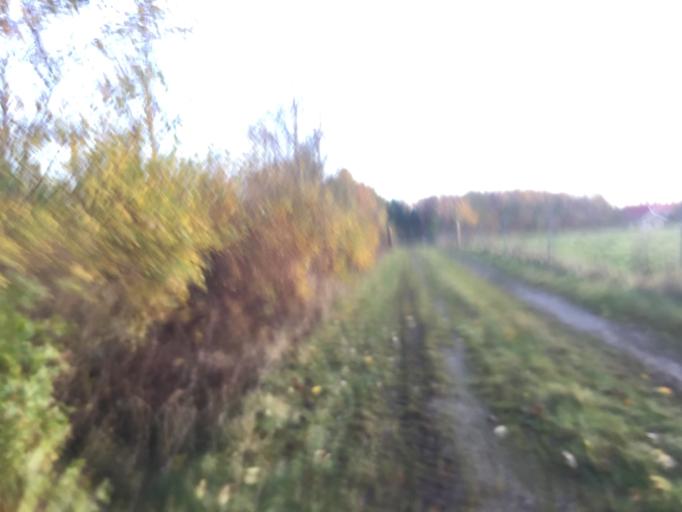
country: DK
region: Zealand
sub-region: Ringsted Kommune
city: Ringsted
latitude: 55.4719
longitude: 11.7695
